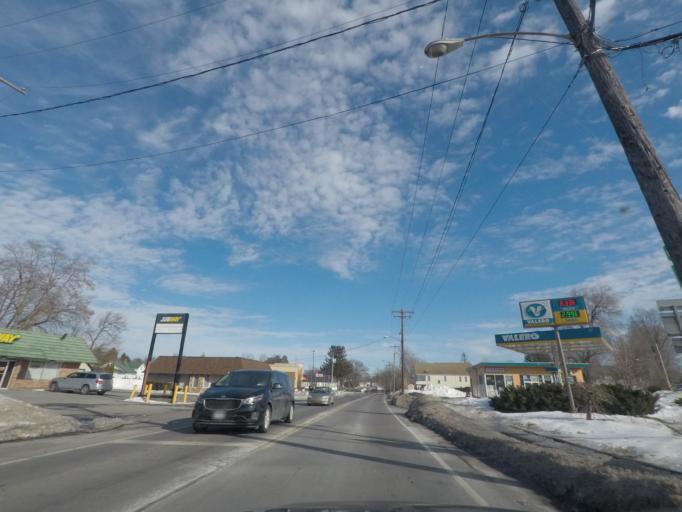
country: US
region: New York
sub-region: Schenectady County
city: Rotterdam
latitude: 42.7900
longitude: -73.9799
